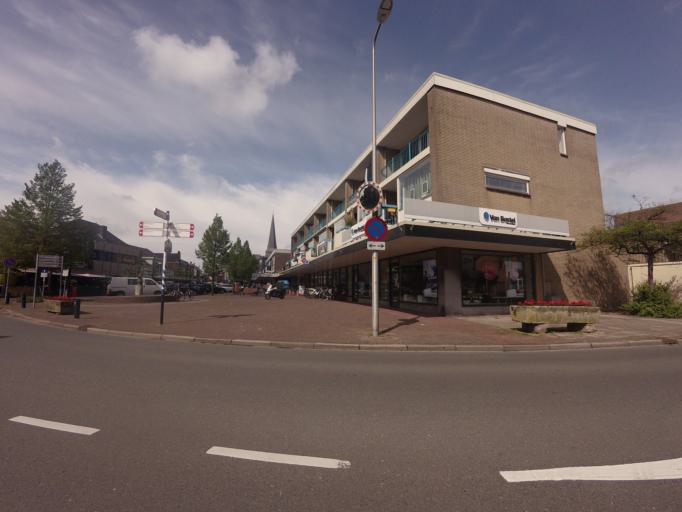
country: NL
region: Overijssel
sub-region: Gemeente Haaksbergen
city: Haaksbergen
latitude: 52.1530
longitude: 6.7415
